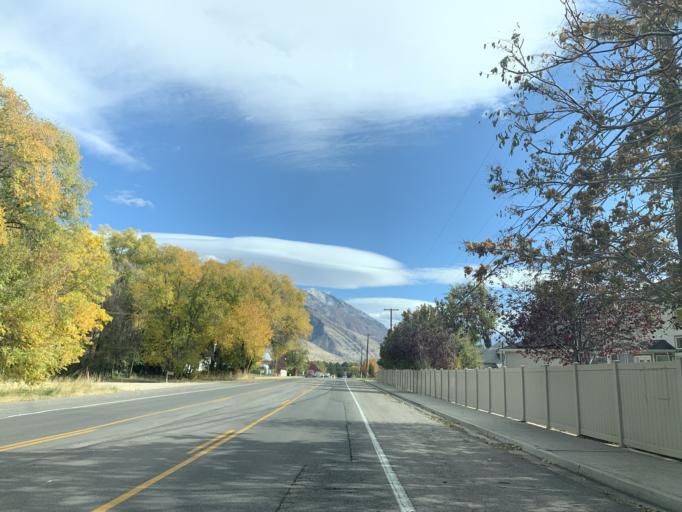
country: US
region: Utah
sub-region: Utah County
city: Provo
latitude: 40.2595
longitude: -111.6794
